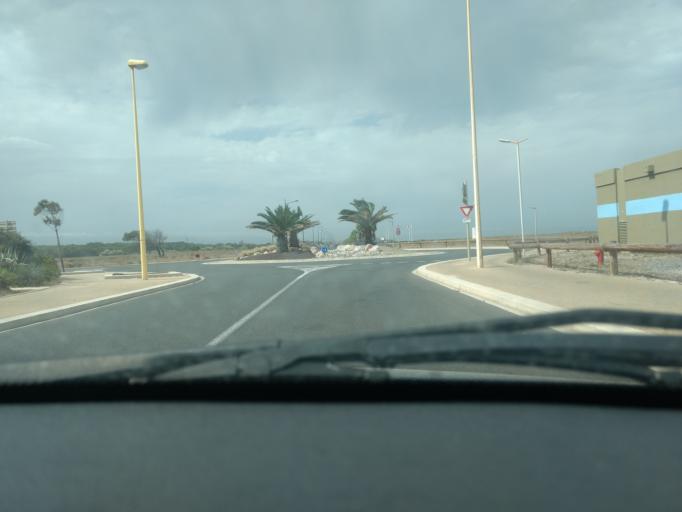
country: FR
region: Languedoc-Roussillon
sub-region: Departement des Pyrenees-Orientales
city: Le Barcares
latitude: 42.8113
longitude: 3.0379
